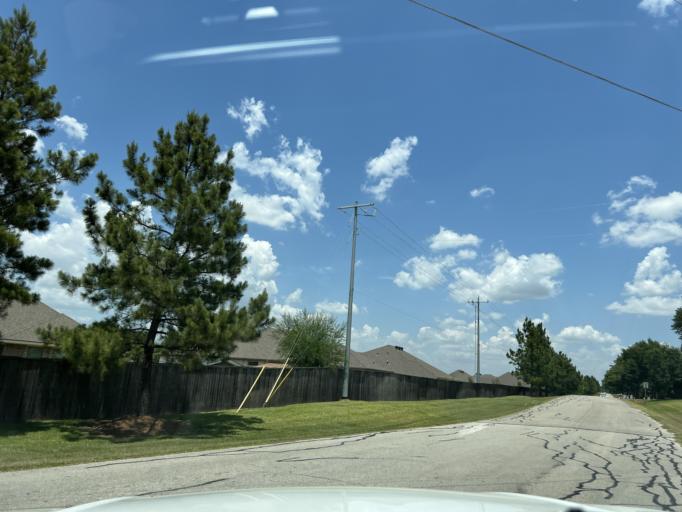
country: US
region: Texas
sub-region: Washington County
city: Brenham
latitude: 30.1509
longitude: -96.3745
